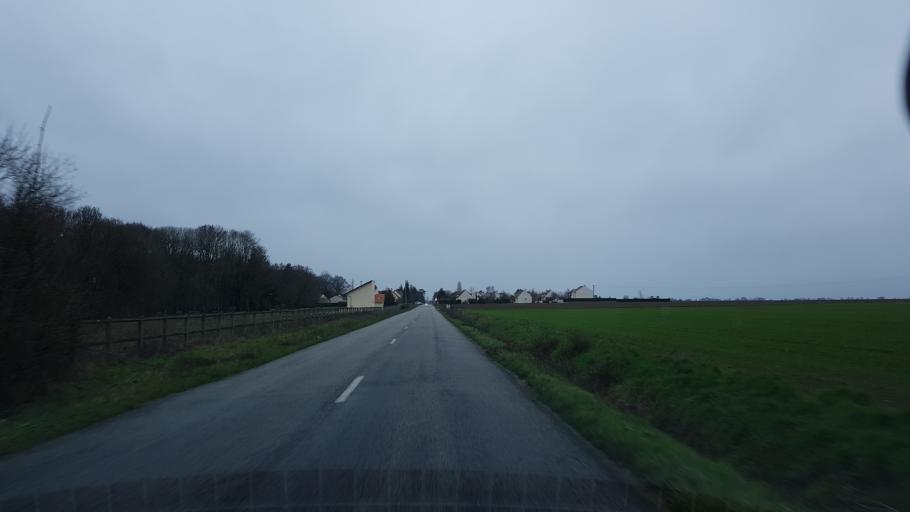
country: FR
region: Ile-de-France
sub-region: Departement de l'Essonne
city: Forges-les-Bains
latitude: 48.6444
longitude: 2.1150
